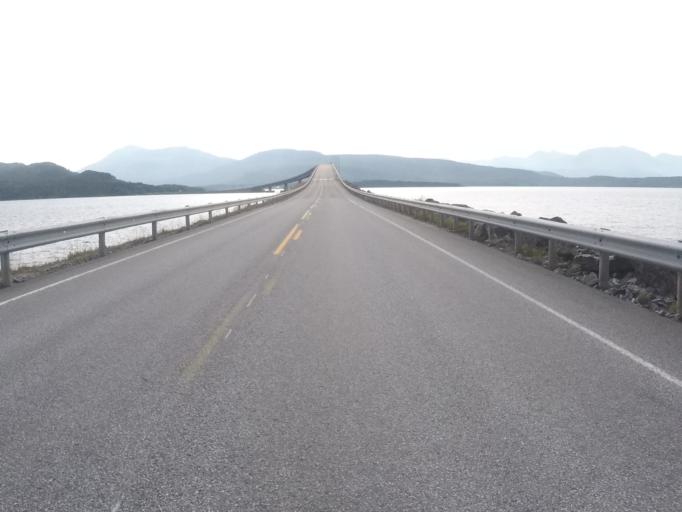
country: NO
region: More og Romsdal
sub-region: Molde
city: Hjelset
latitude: 62.7318
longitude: 7.3457
